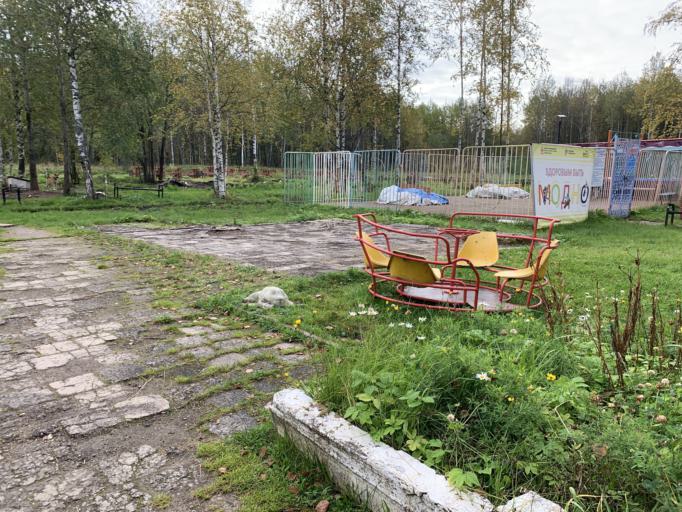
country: RU
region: Perm
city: Gubakha
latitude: 58.8331
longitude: 57.5633
